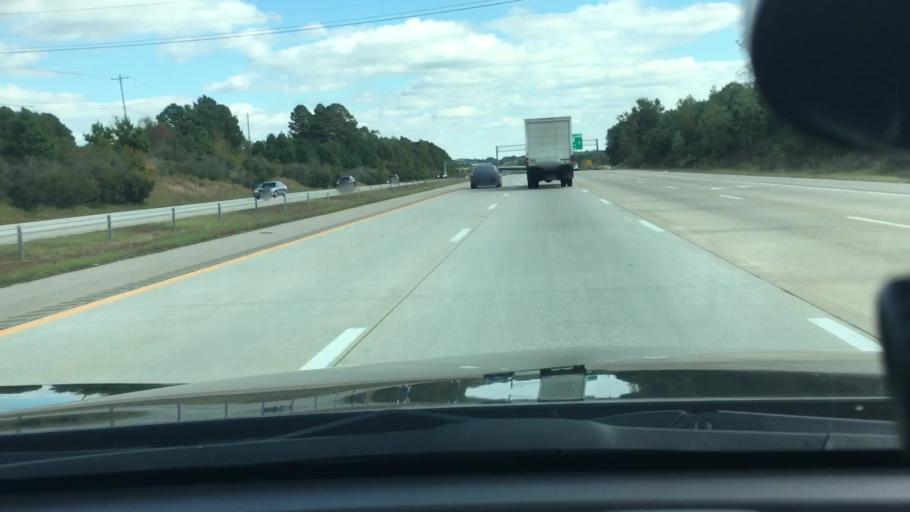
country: US
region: North Carolina
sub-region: Wake County
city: Knightdale
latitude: 35.7681
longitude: -78.5184
